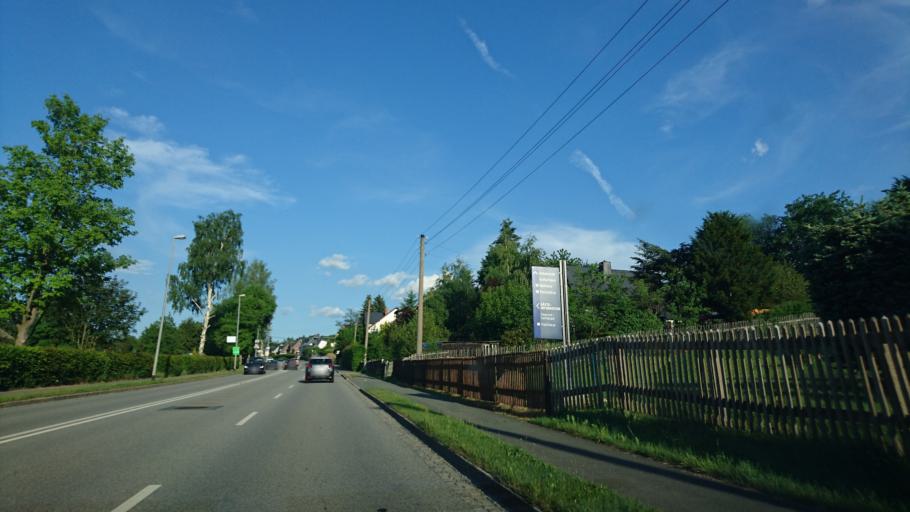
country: DE
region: Saxony
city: Schlema
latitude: 50.5975
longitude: 12.6613
